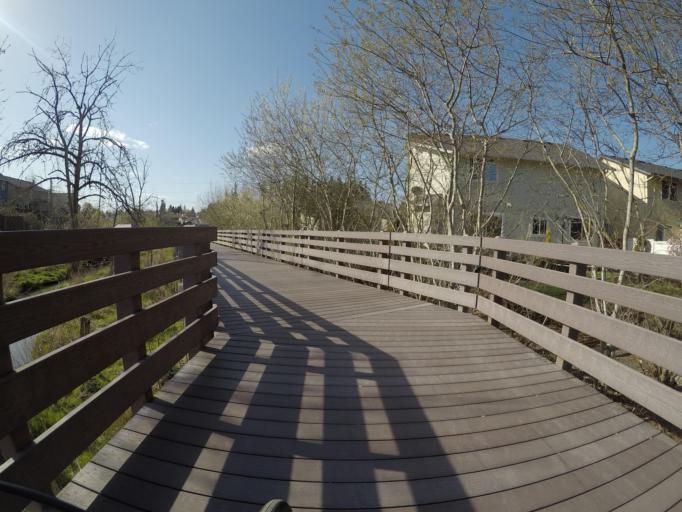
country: US
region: Oregon
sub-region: Washington County
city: Bethany
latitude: 45.5582
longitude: -122.8548
